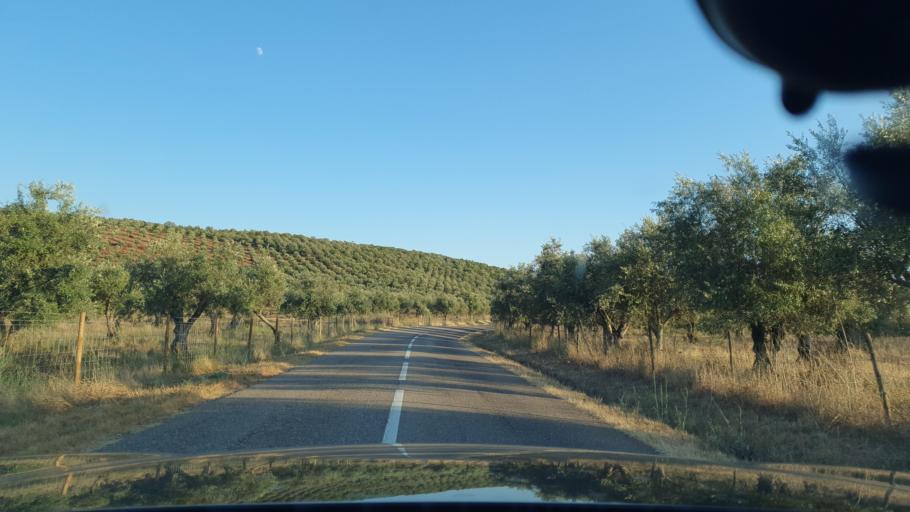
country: PT
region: Evora
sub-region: Estremoz
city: Estremoz
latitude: 38.9289
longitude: -7.6657
